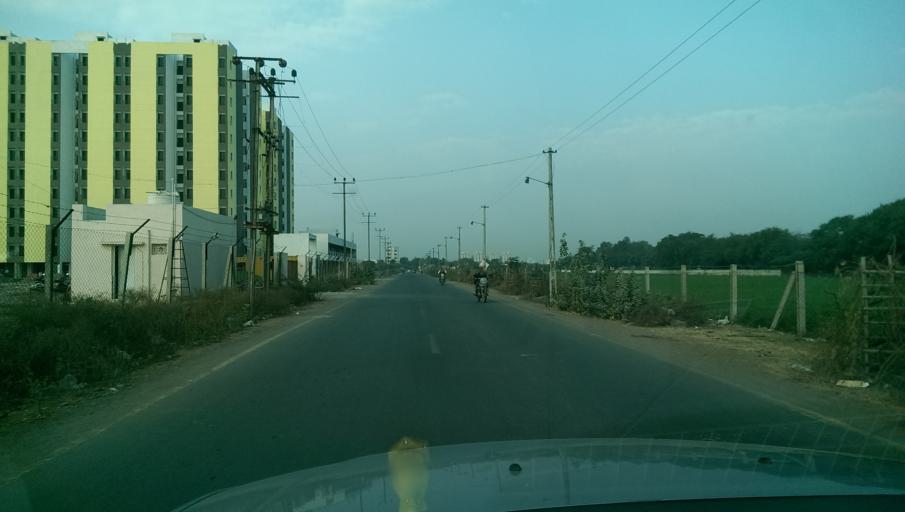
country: IN
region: Gujarat
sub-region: Jamnagar
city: Jamnagar
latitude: 22.4766
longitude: 70.0496
